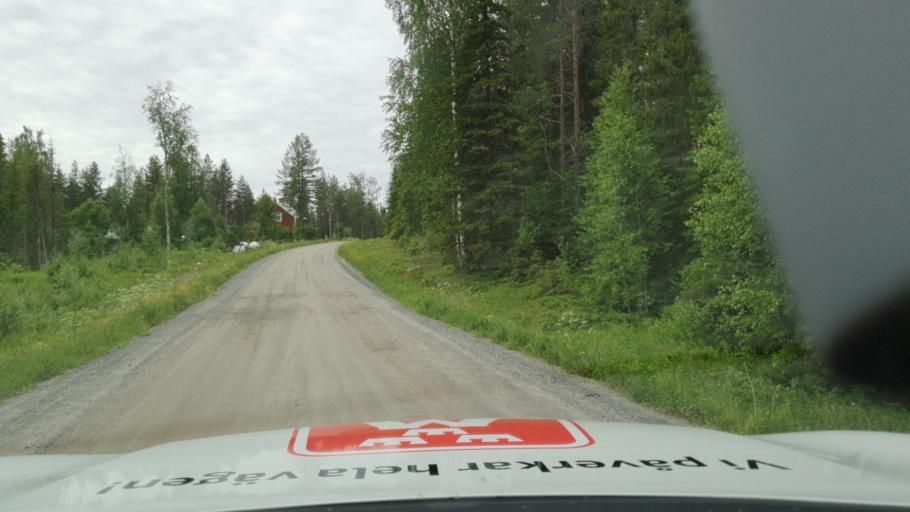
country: SE
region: Vaesterbotten
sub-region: Skelleftea Kommun
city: Langsele
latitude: 64.4846
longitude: 20.2519
